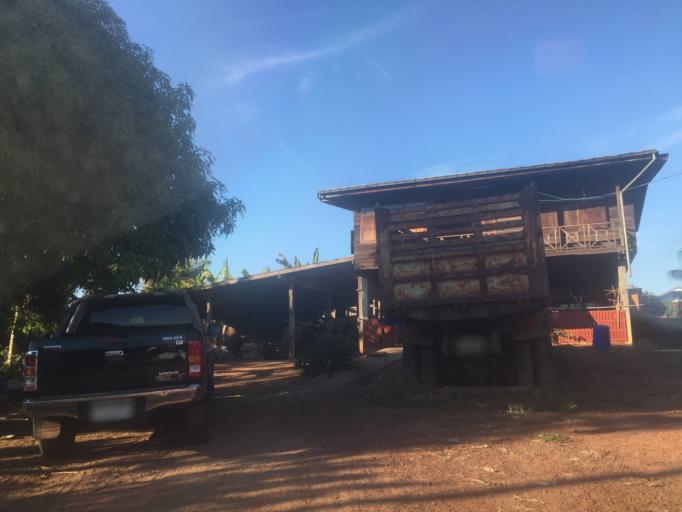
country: TH
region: Changwat Udon Thani
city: Si That
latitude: 16.9854
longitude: 103.2611
